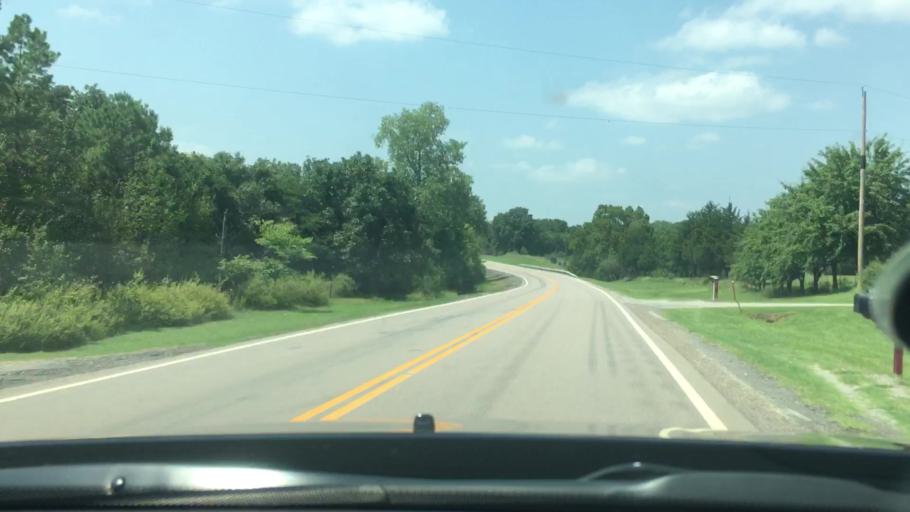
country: US
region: Oklahoma
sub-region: Coal County
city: Coalgate
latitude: 34.3726
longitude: -96.3876
